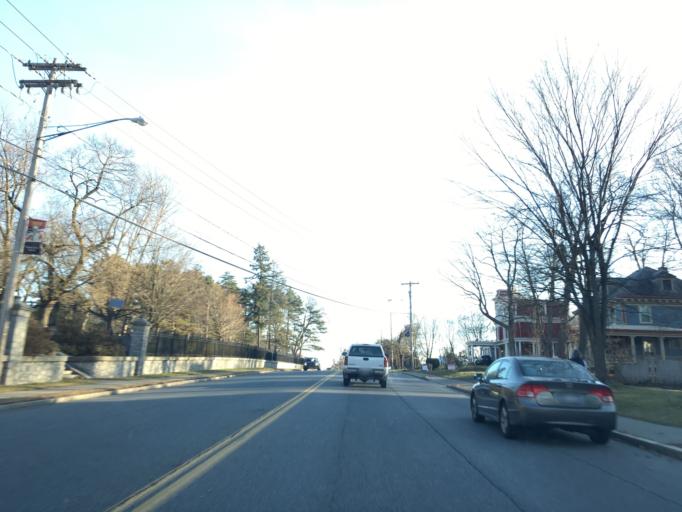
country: US
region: New York
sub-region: Rensselaer County
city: Wynantskill
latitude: 42.7121
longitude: -73.6657
